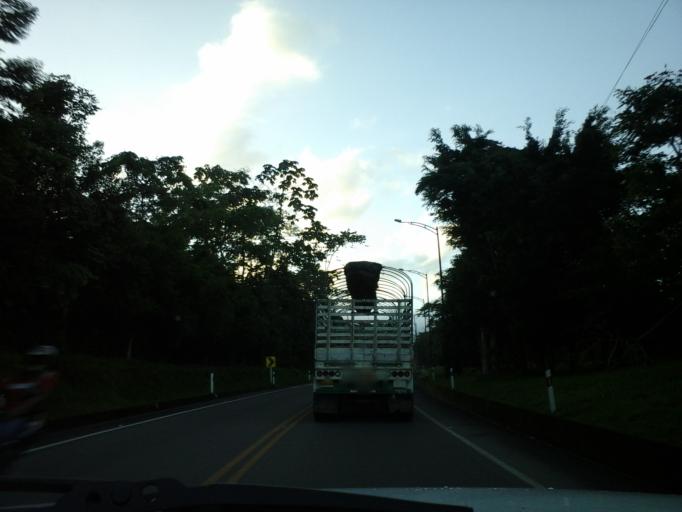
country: CO
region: Meta
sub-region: Villavicencio
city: Villavicencio
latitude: 4.1293
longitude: -73.6540
